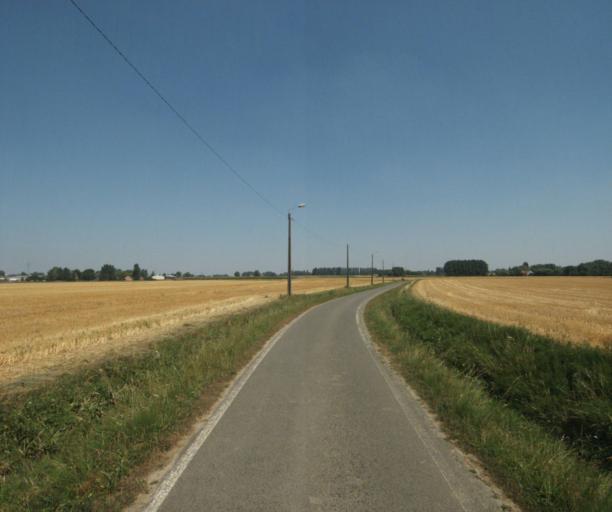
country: FR
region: Nord-Pas-de-Calais
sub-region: Departement du Nord
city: Wervicq-Sud
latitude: 50.7454
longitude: 3.0452
